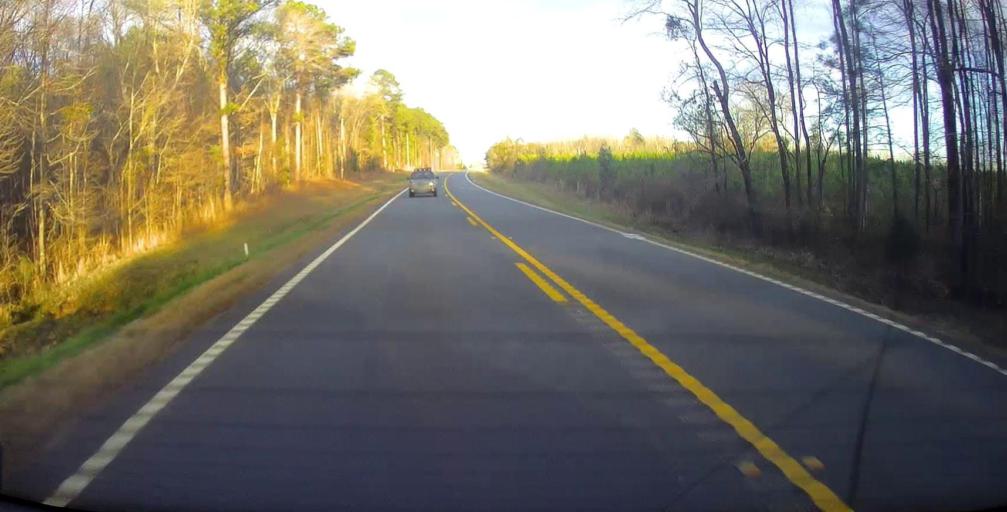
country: US
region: Georgia
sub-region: Talbot County
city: Sardis
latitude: 32.7195
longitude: -84.6711
